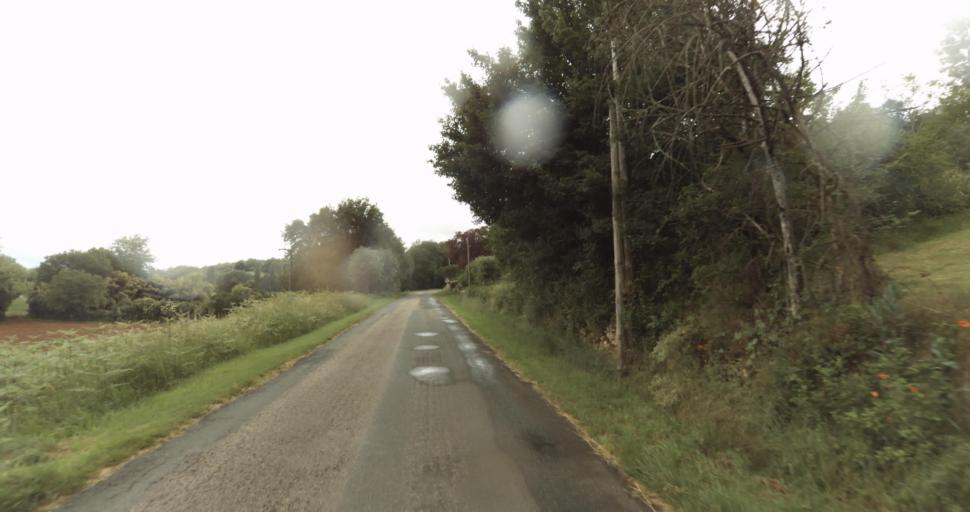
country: FR
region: Aquitaine
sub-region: Departement de la Dordogne
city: Belves
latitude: 44.7561
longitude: 0.9235
